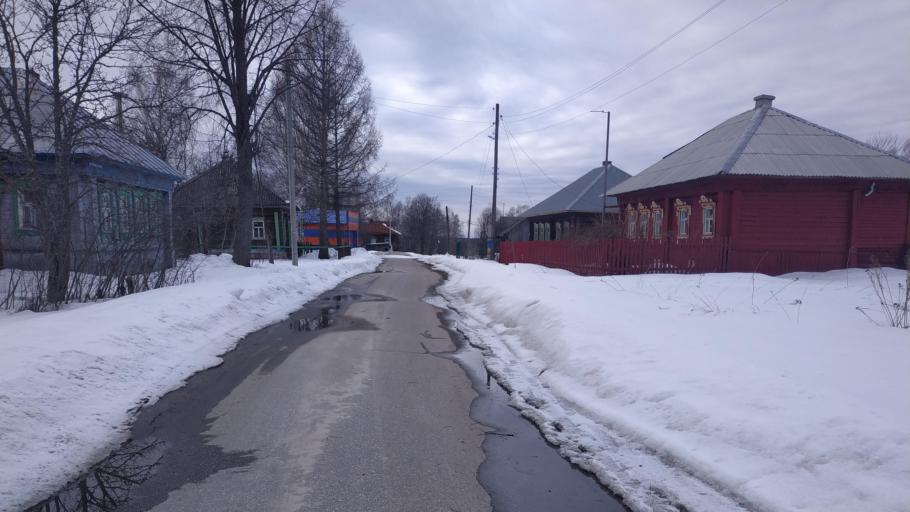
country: RU
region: Nizjnij Novgorod
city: Semenov
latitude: 56.7755
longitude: 44.2886
